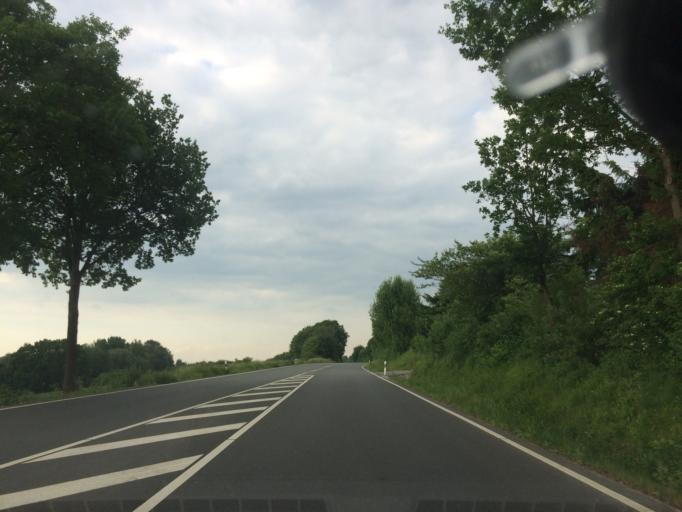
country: DE
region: Hesse
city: Trendelburg
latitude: 51.5485
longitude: 9.4150
